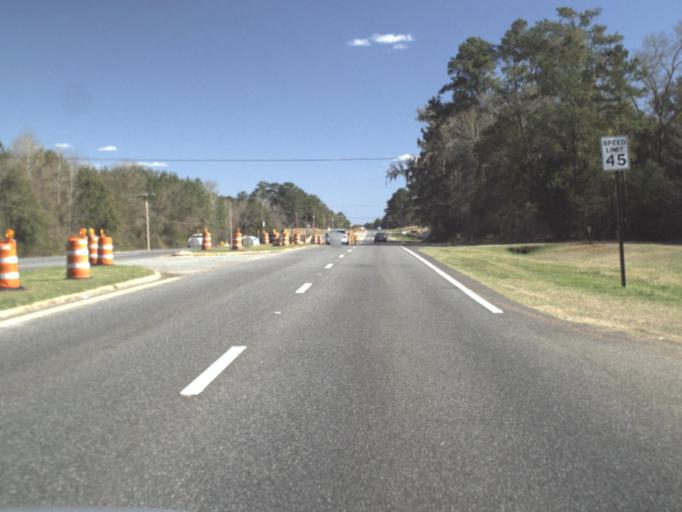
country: US
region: Florida
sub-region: Gadsden County
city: Quincy
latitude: 30.5732
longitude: -84.5522
